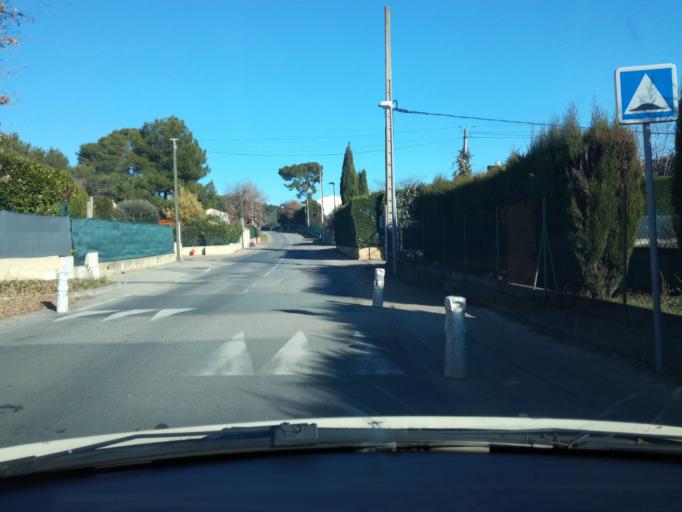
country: FR
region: Provence-Alpes-Cote d'Azur
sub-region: Departement des Alpes-Maritimes
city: La Roquette-sur-Siagne
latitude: 43.6046
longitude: 6.9545
